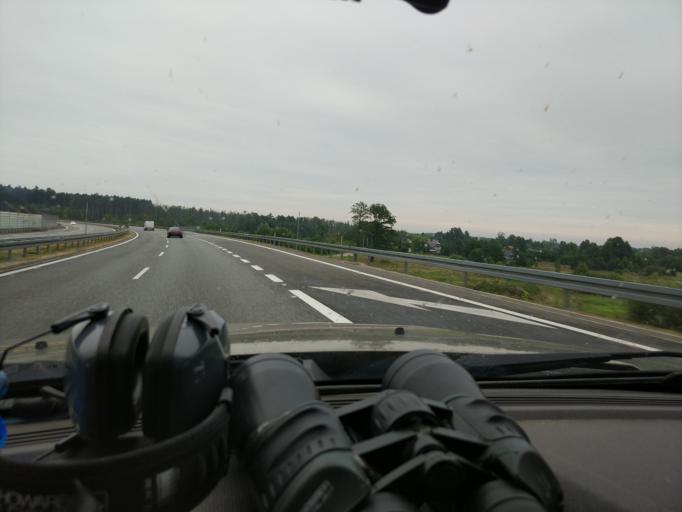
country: PL
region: Masovian Voivodeship
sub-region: Powiat wyszkowski
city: Wyszkow
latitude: 52.5583
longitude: 21.4647
